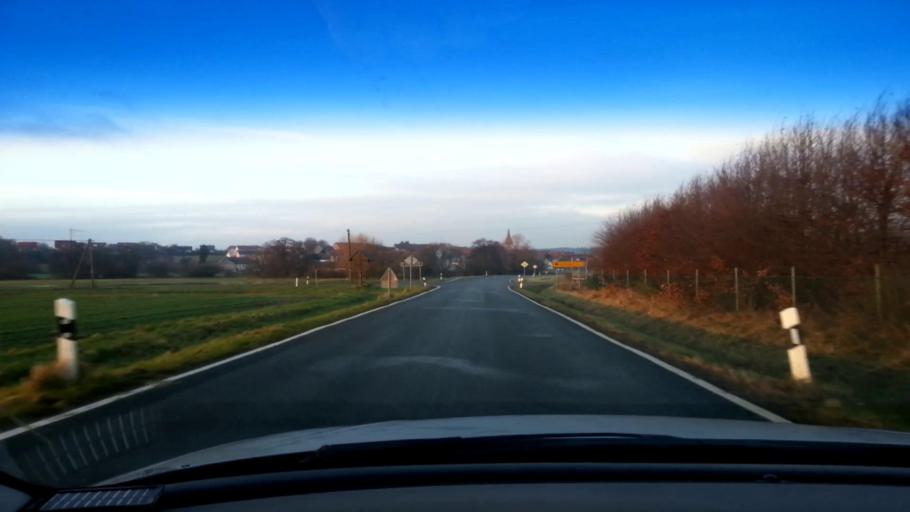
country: DE
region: Bavaria
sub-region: Upper Franconia
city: Frensdorf
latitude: 49.7874
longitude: 10.8867
